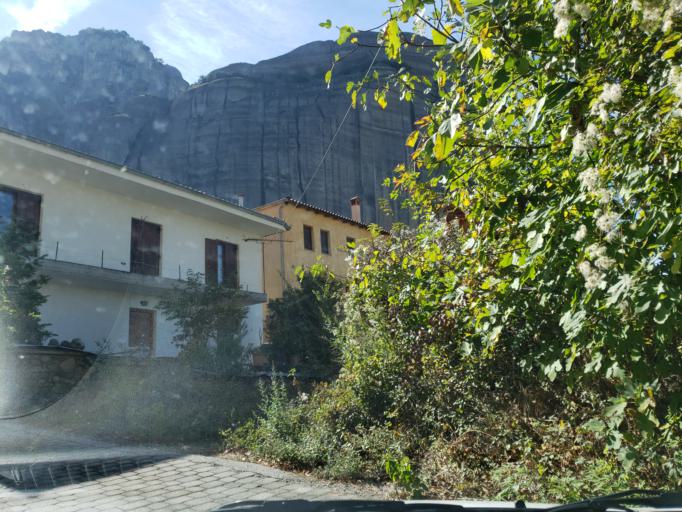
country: GR
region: Thessaly
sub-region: Trikala
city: Kastraki
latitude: 39.7160
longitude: 21.6237
